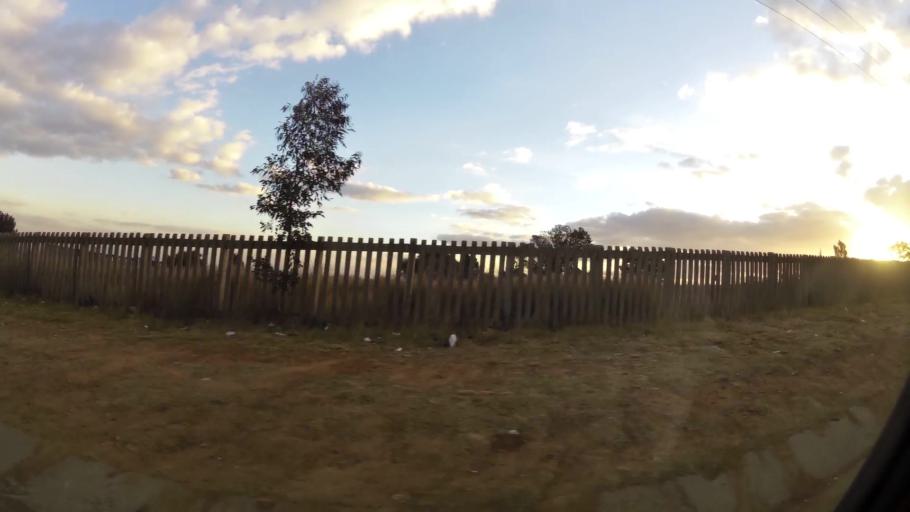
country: ZA
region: Gauteng
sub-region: City of Johannesburg Metropolitan Municipality
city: Midrand
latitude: -26.0003
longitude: 28.1405
